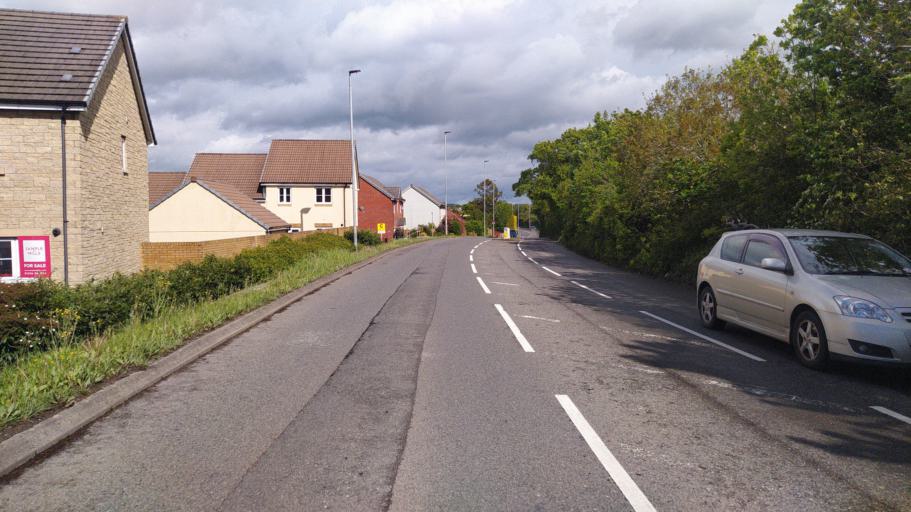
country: GB
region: England
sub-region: Devon
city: Newton Abbot
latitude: 50.5366
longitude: -3.6426
